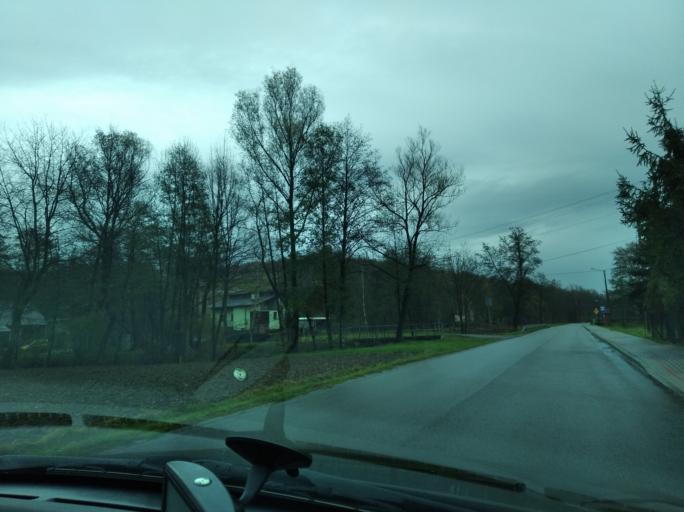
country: PL
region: Subcarpathian Voivodeship
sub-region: Powiat rzeszowski
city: Straszydle
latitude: 49.9125
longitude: 21.9606
